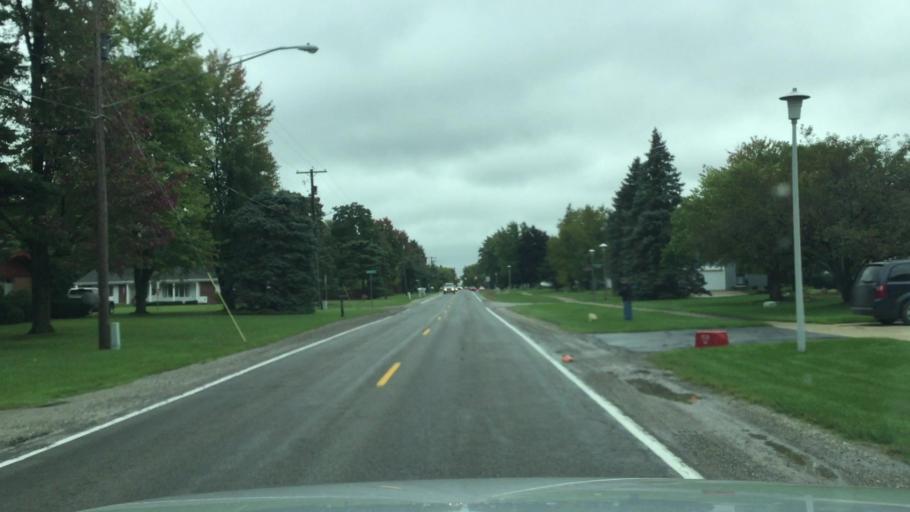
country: US
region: Michigan
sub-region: Saginaw County
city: Shields
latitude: 43.4550
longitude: -84.0052
